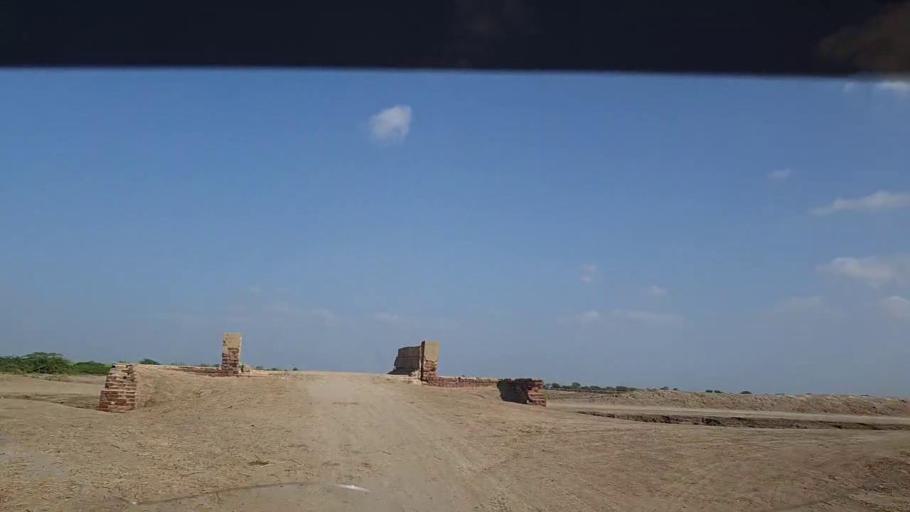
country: PK
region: Sindh
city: Kadhan
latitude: 24.4564
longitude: 68.8582
